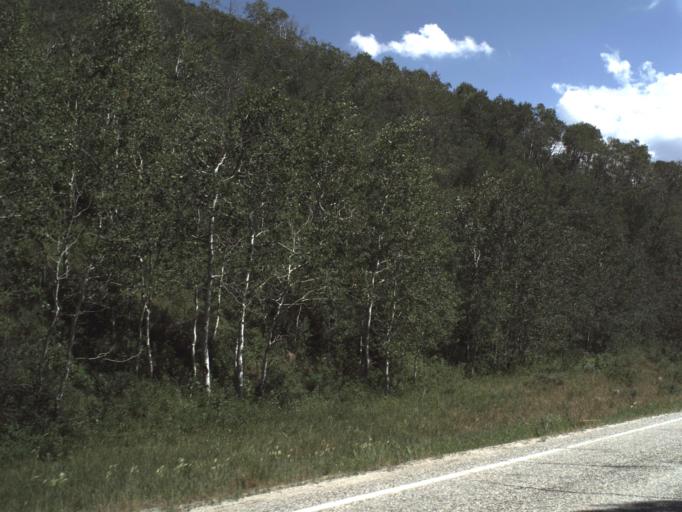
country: US
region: Utah
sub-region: Weber County
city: Wolf Creek
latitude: 41.4004
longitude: -111.5993
